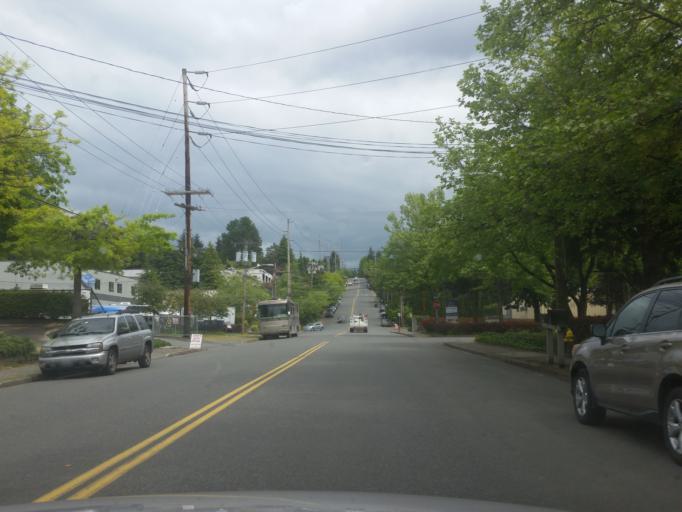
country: US
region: Washington
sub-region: King County
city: Kirkland
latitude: 47.6806
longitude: -122.1948
